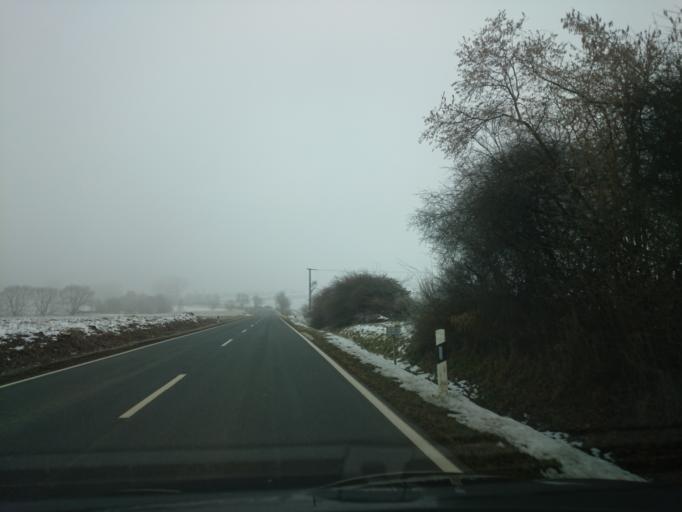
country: DE
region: Bavaria
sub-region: Regierungsbezirk Mittelfranken
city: Thalmassing
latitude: 49.1196
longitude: 11.2727
